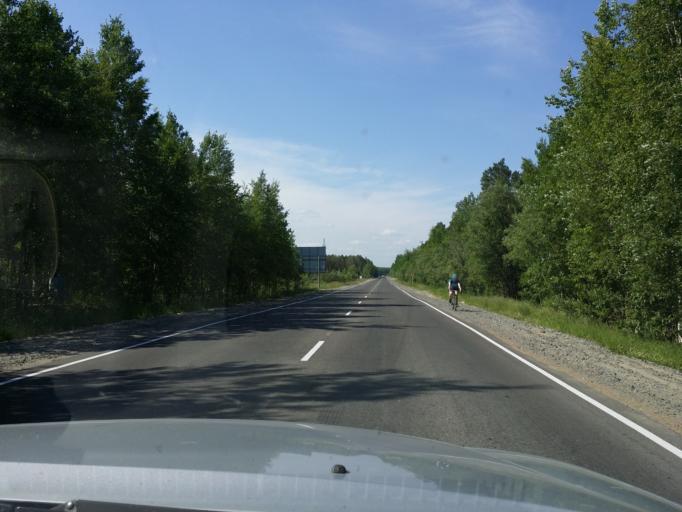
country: RU
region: Khanty-Mansiyskiy Avtonomnyy Okrug
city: Izluchinsk
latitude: 60.9411
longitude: 76.8592
